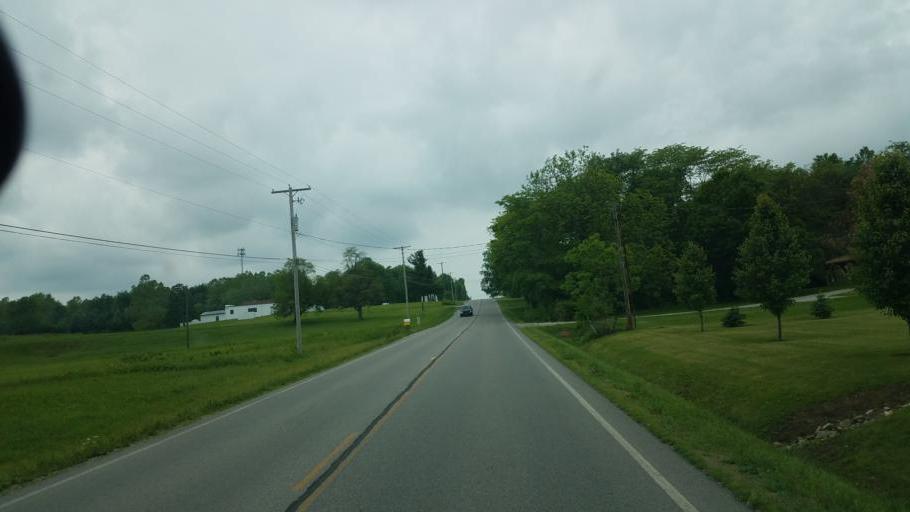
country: US
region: Ohio
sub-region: Delaware County
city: Delaware
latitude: 40.3203
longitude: -83.1323
